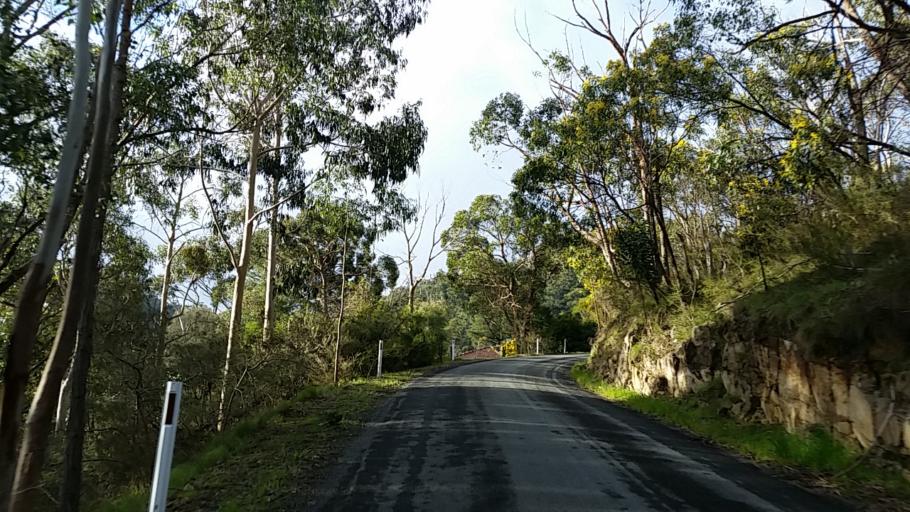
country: AU
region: South Australia
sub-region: Adelaide Hills
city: Adelaide Hills
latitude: -34.9285
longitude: 138.7767
